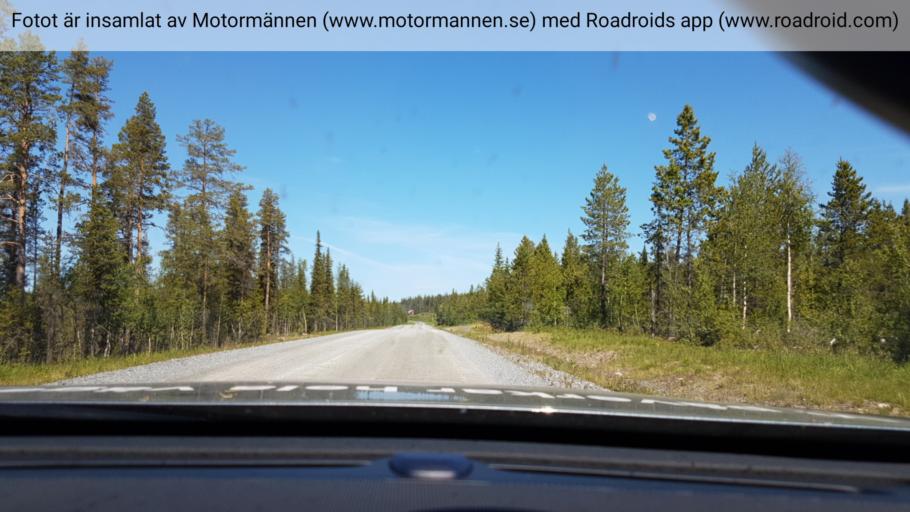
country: SE
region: Vaesterbotten
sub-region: Vilhelmina Kommun
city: Sjoberg
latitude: 64.6815
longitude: 15.7525
